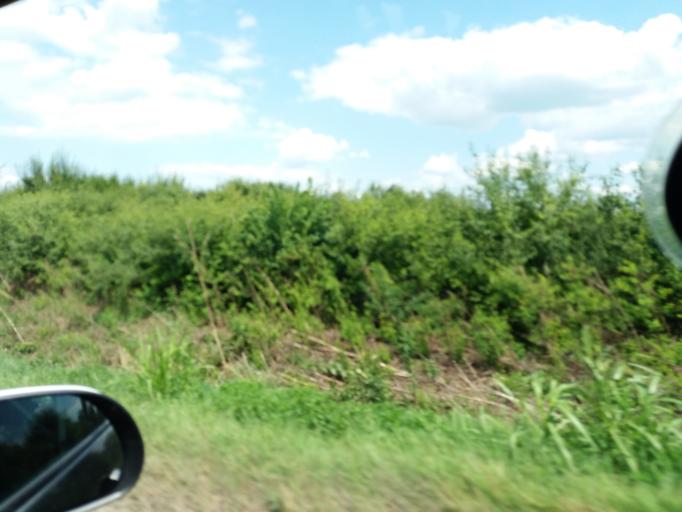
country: RS
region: Autonomna Pokrajina Vojvodina
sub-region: Sremski Okrug
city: Pecinci
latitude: 44.8571
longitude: 19.9604
